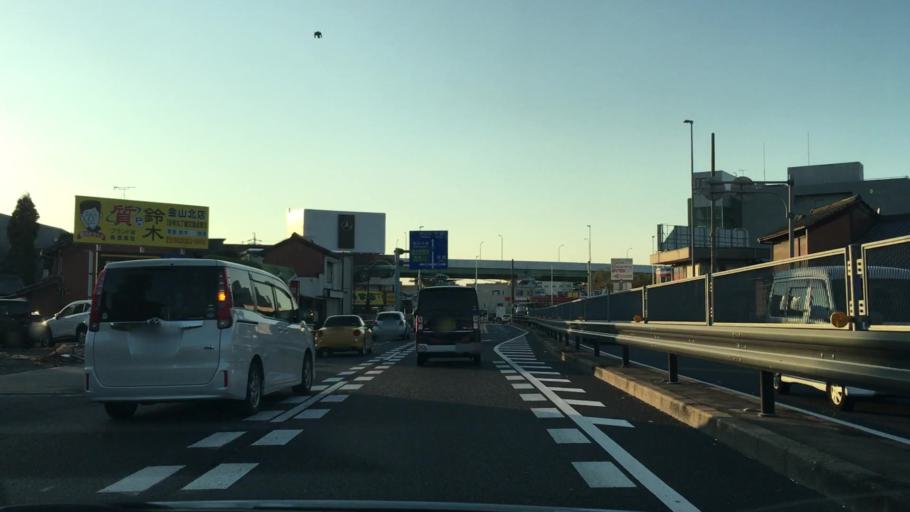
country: JP
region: Aichi
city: Obu
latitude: 35.0839
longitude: 136.9357
